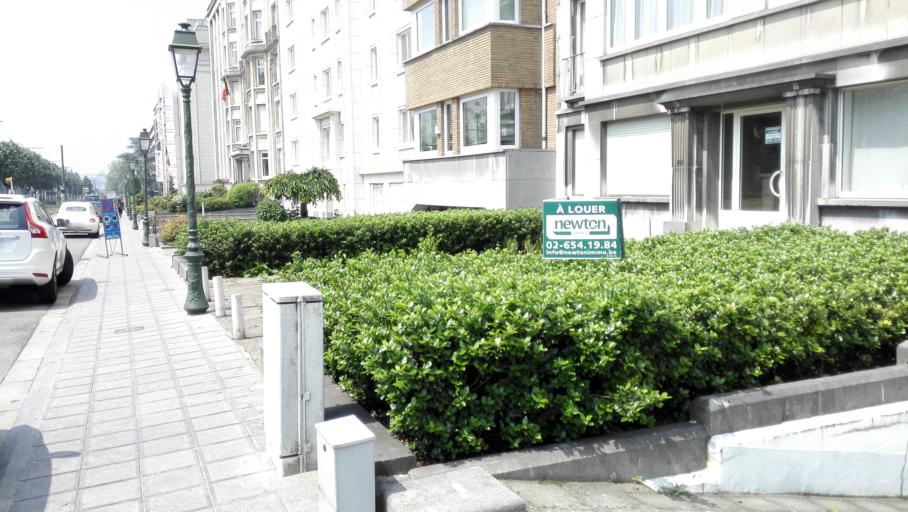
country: BE
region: Flanders
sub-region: Provincie Vlaams-Brabant
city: Kraainem
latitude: 50.8363
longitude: 4.4140
